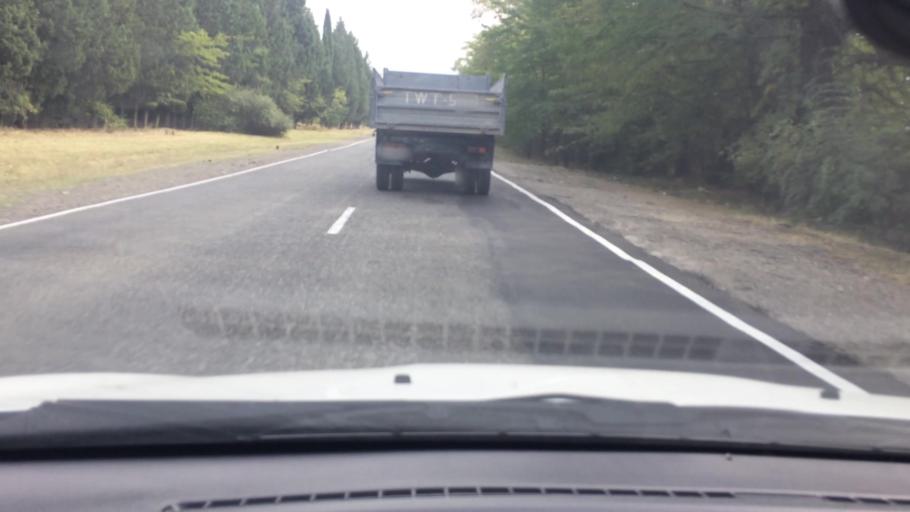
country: GE
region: Kvemo Kartli
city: Rust'avi
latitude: 41.4668
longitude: 44.9820
